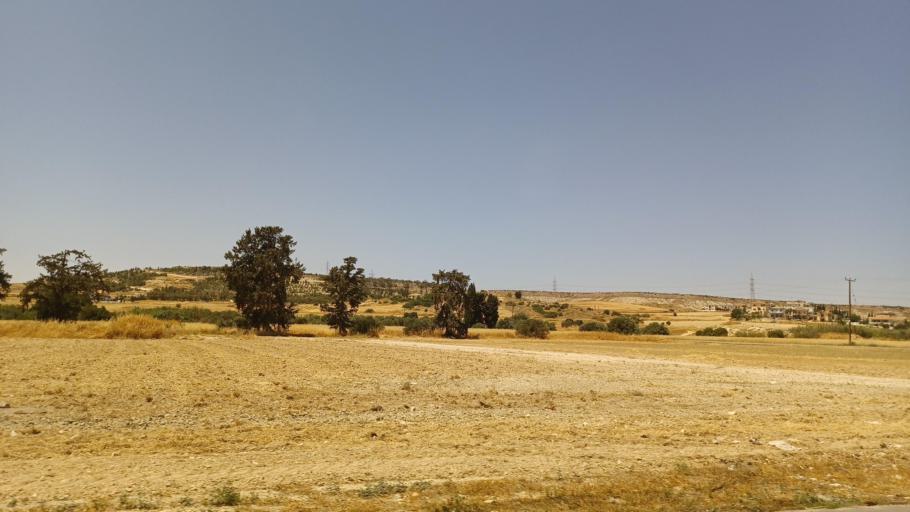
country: CY
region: Larnaka
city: Pyla
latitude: 34.9985
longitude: 33.6880
